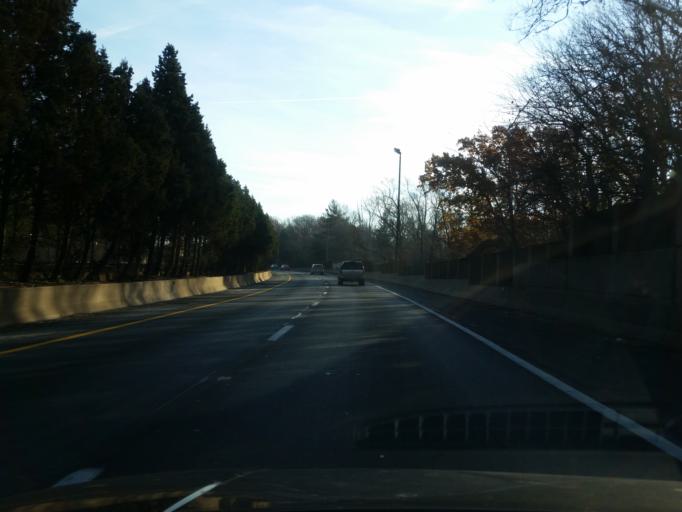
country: US
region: Virginia
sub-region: Fairfax County
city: Seven Corners
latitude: 38.8795
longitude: -77.1378
